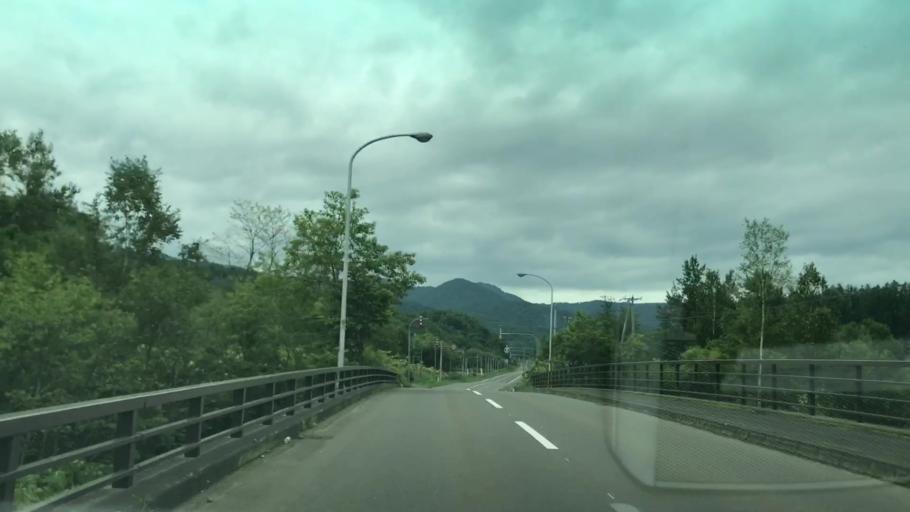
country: JP
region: Hokkaido
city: Yoichi
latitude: 43.0596
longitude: 140.8213
